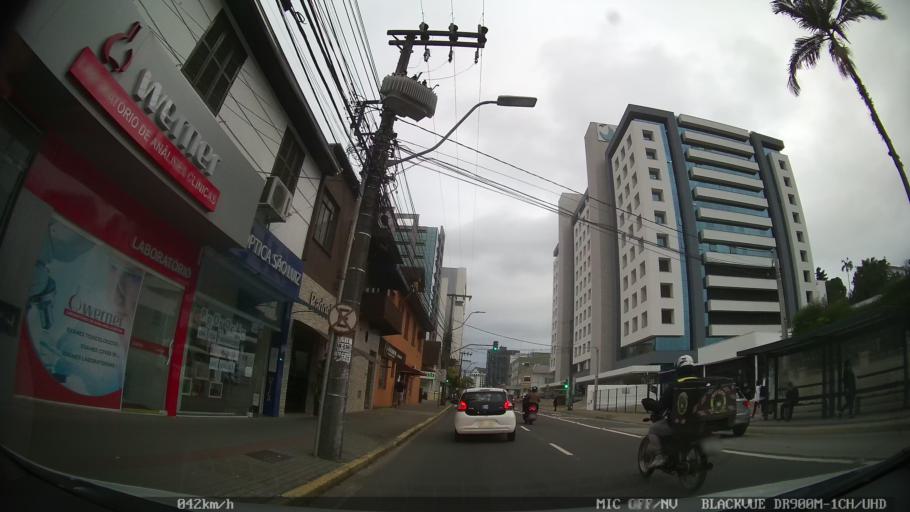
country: BR
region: Santa Catarina
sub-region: Joinville
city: Joinville
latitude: -26.2979
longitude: -48.8504
